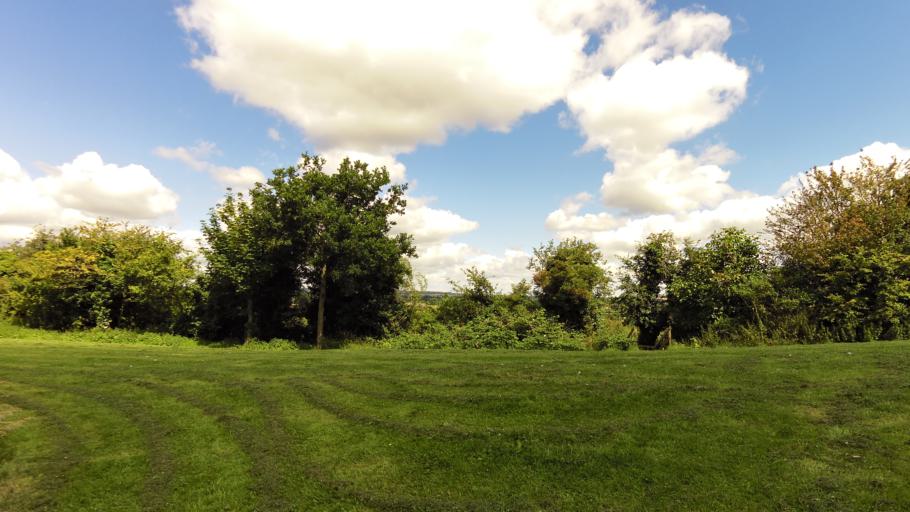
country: GB
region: England
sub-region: Wiltshire
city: Devizes
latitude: 51.3532
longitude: -2.0248
